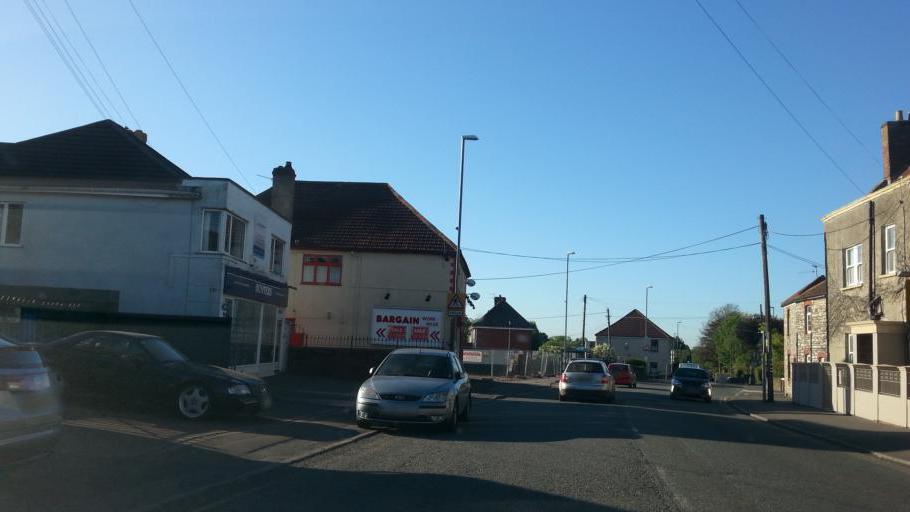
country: GB
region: England
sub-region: Bath and North East Somerset
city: Whitchurch
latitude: 51.4068
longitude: -2.5586
